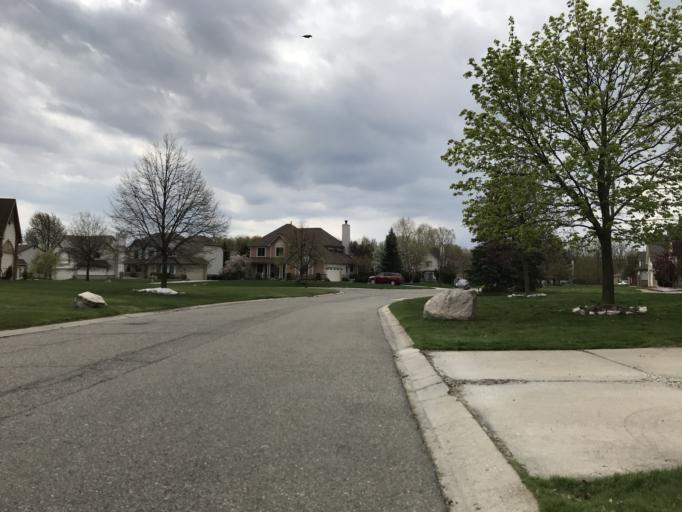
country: US
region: Michigan
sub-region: Oakland County
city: Farmington
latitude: 42.4693
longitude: -83.3339
